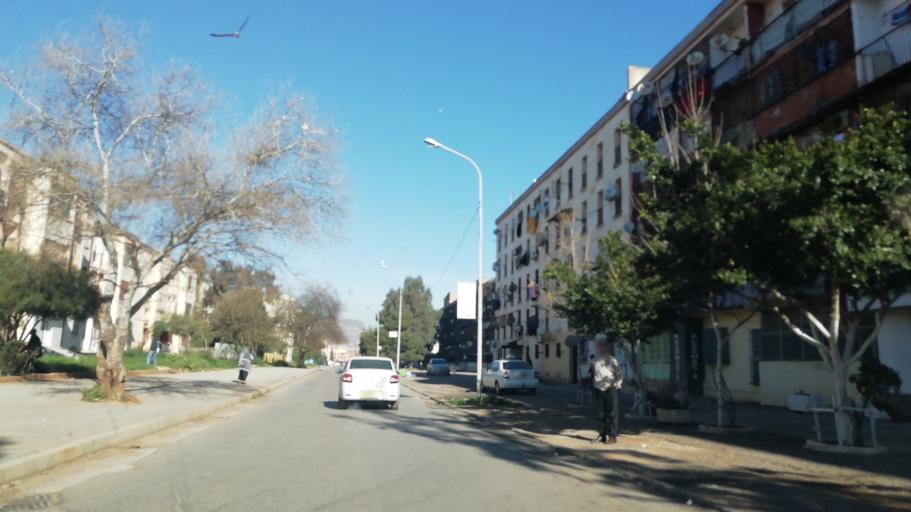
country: DZ
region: Oran
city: Oran
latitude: 35.6691
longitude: -0.6466
